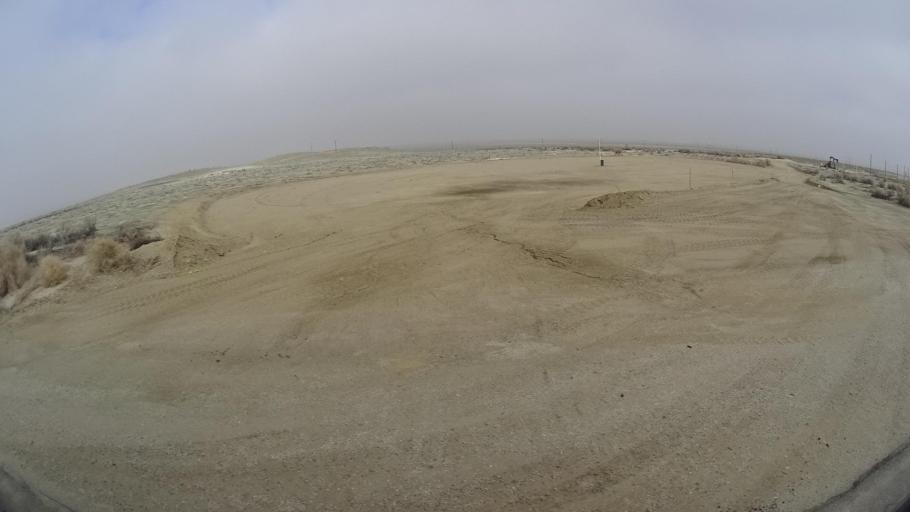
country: US
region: California
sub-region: Kern County
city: Maricopa
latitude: 35.0354
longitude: -119.3542
